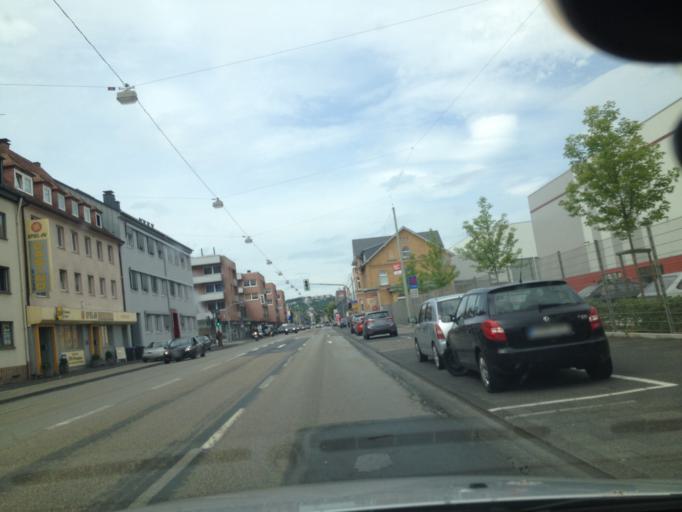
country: DE
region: North Rhine-Westphalia
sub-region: Regierungsbezirk Arnsberg
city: Siegen
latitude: 50.8857
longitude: 8.0291
